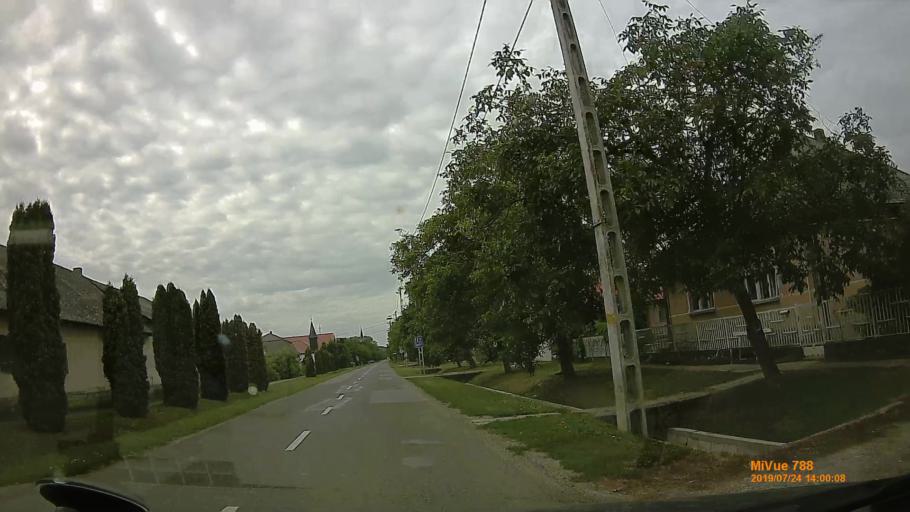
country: HU
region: Szabolcs-Szatmar-Bereg
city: Aranyosapati
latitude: 48.2586
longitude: 22.3057
